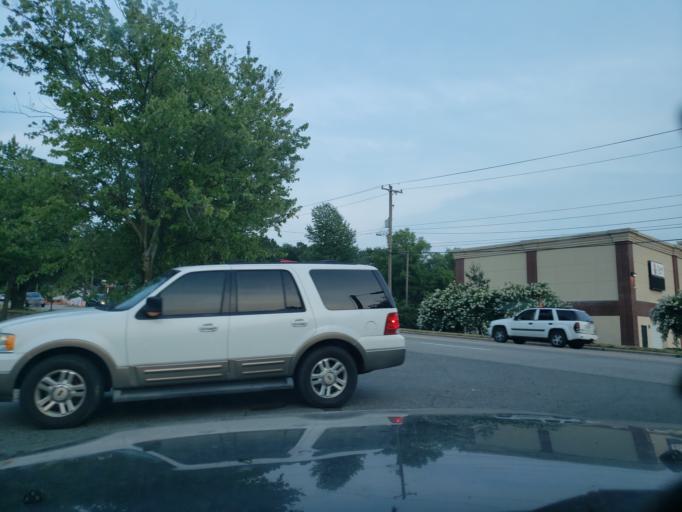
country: US
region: North Carolina
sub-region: Durham County
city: Durham
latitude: 35.9926
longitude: -78.8679
